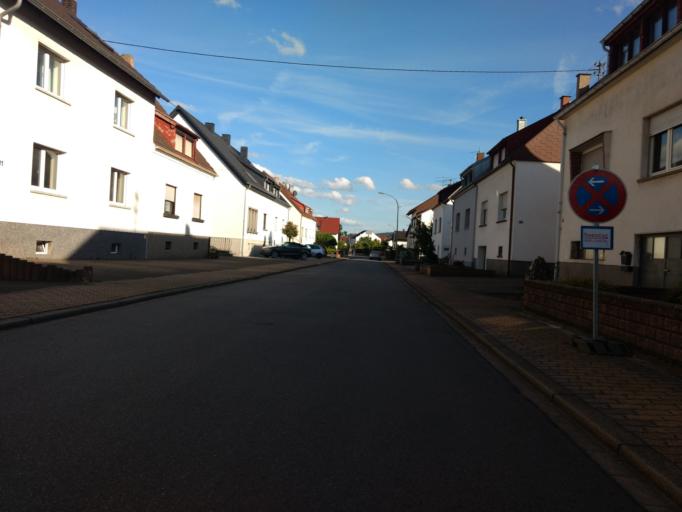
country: DE
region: Saarland
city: Rehlingen-Siersburg
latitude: 49.3762
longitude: 6.6823
